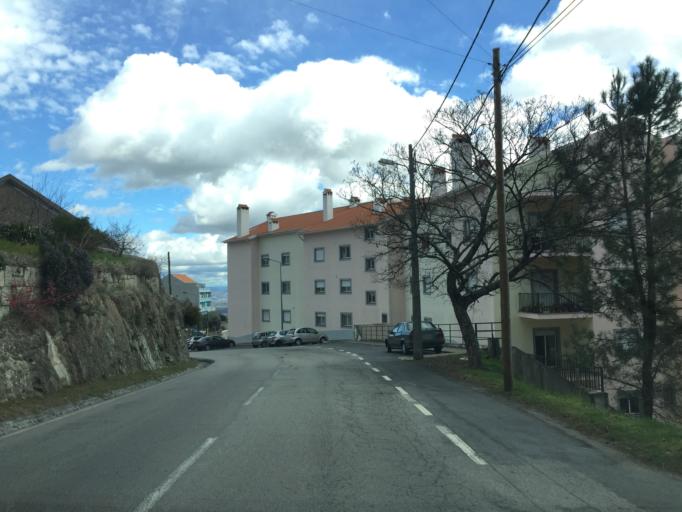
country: PT
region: Castelo Branco
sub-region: Covilha
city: Covilha
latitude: 40.2811
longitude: -7.5135
